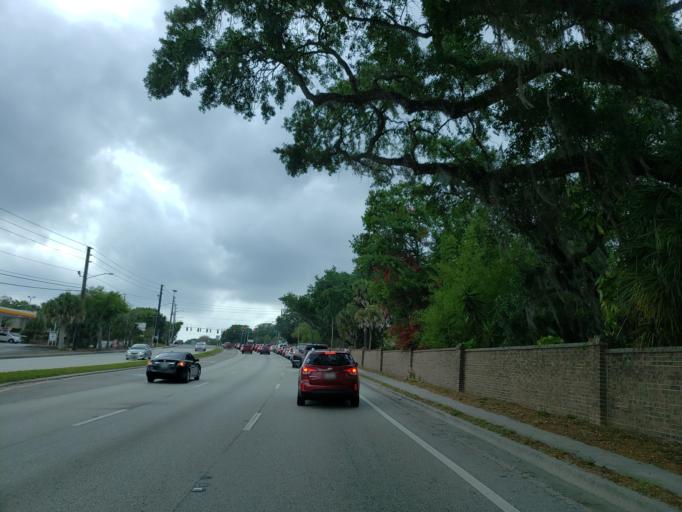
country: US
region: Florida
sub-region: Pinellas County
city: Saint George
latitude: 28.0674
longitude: -82.7203
